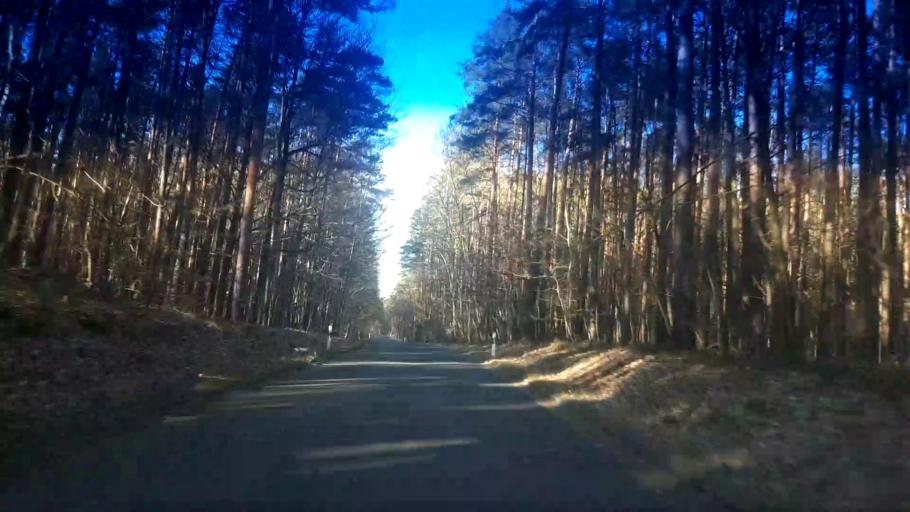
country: DE
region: Bavaria
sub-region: Upper Franconia
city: Lauter
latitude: 49.9586
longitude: 10.7616
